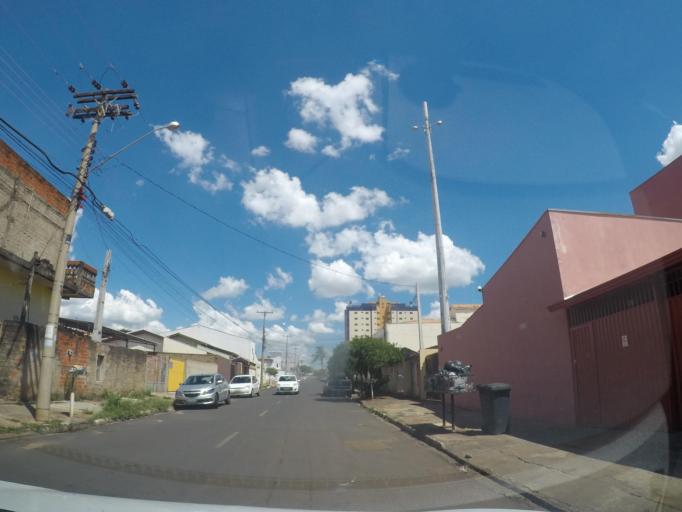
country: BR
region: Sao Paulo
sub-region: Sumare
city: Sumare
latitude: -22.8301
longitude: -47.2769
